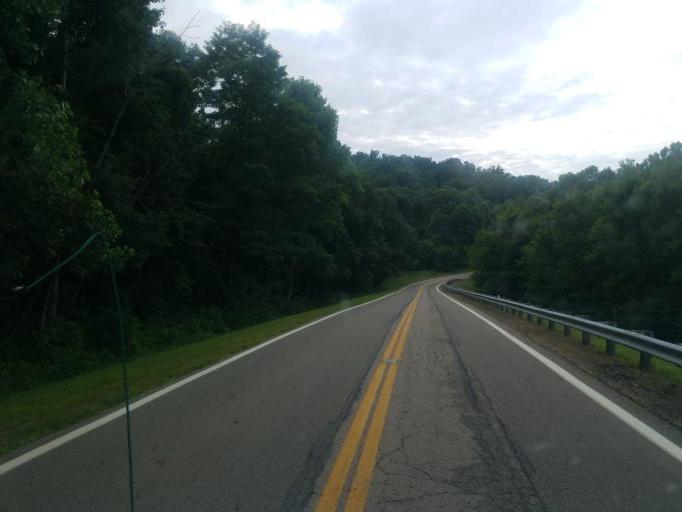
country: US
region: Ohio
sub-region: Knox County
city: Oak Hill
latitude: 40.3485
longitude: -82.0925
